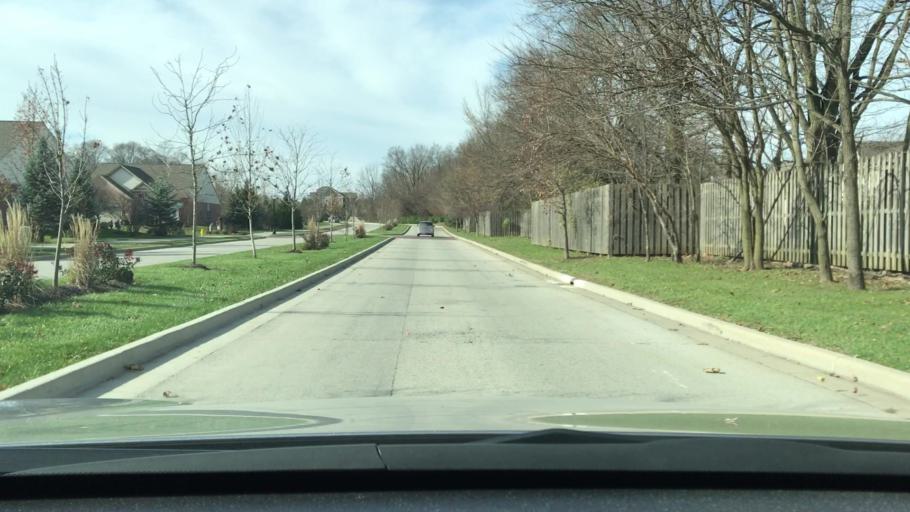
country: US
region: Indiana
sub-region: Hamilton County
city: Carmel
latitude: 39.9929
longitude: -86.0653
